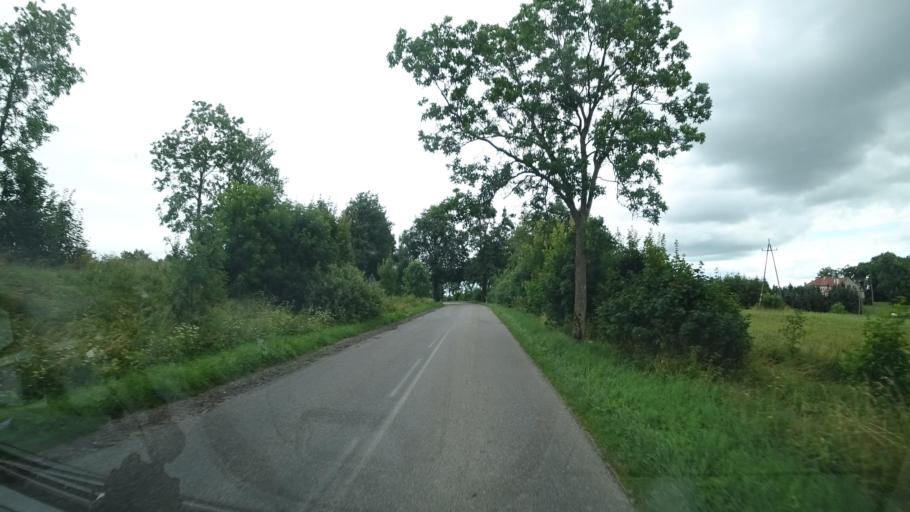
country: PL
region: Podlasie
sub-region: Powiat suwalski
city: Filipow
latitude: 54.2821
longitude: 22.5267
